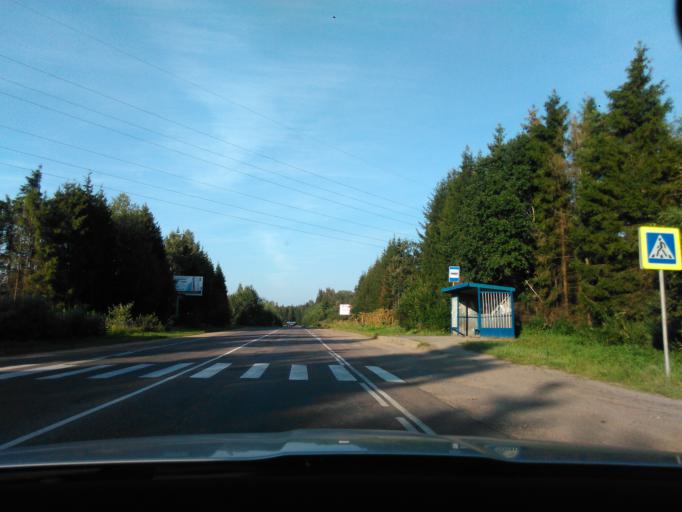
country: RU
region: Tverskaya
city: Konakovo
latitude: 56.6717
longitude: 36.7328
